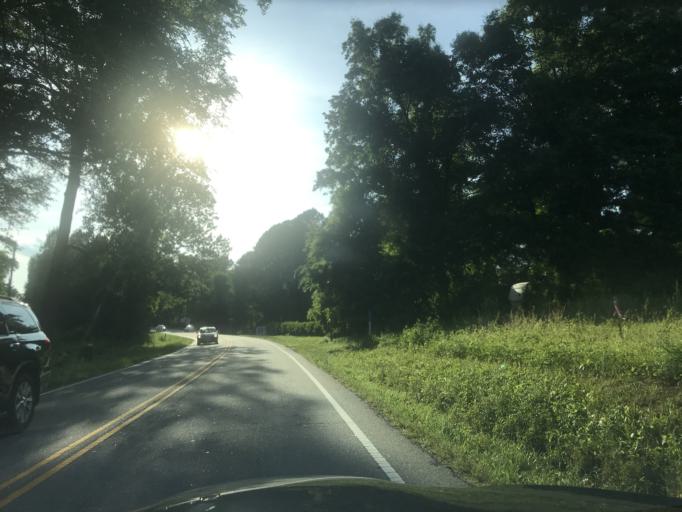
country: US
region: North Carolina
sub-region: Wake County
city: Knightdale
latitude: 35.7548
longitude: -78.5120
